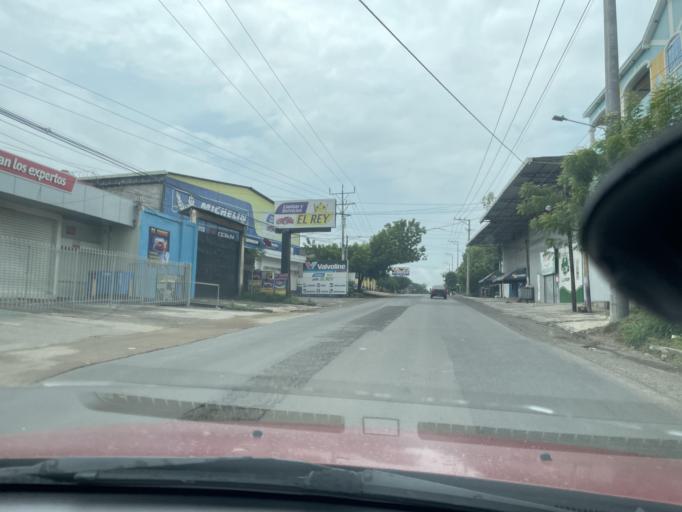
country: SV
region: La Union
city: Santa Rosa de Lima
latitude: 13.6284
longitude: -87.8804
